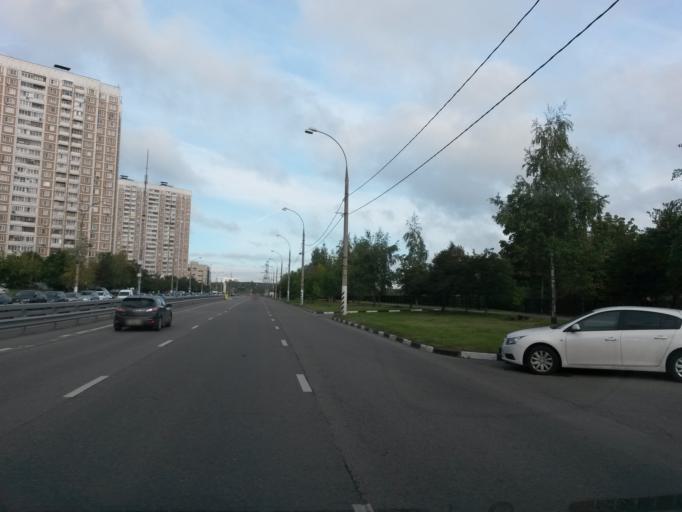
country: RU
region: Moscow
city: Chertanovo Yuzhnoye
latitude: 55.5728
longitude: 37.5734
